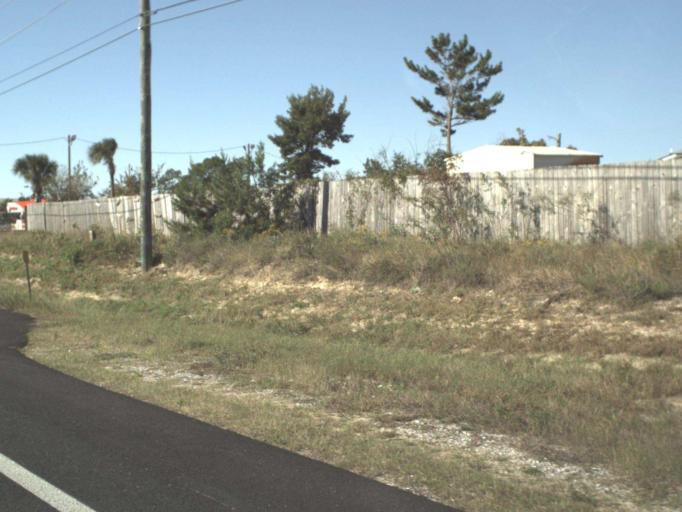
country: US
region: Florida
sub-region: Santa Rosa County
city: Navarre
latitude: 30.4020
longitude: -86.9033
